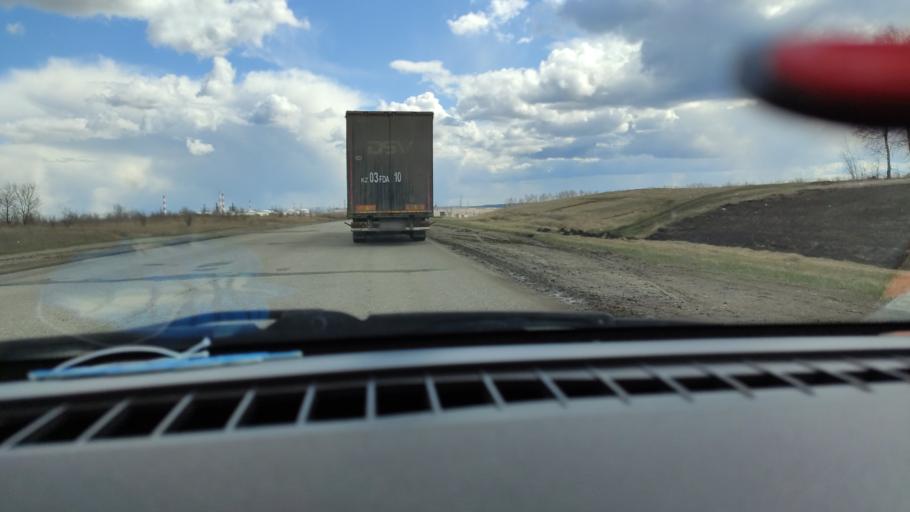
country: RU
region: Samara
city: Varlamovo
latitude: 53.1085
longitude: 48.3557
